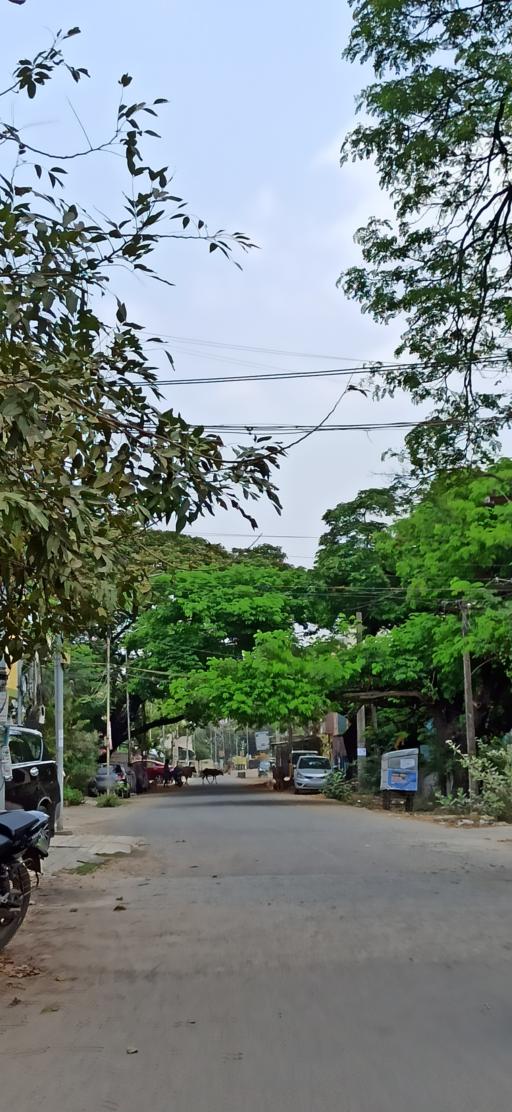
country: IN
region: Tamil Nadu
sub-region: Kancheepuram
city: Manappakkam
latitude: 13.0164
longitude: 80.1482
